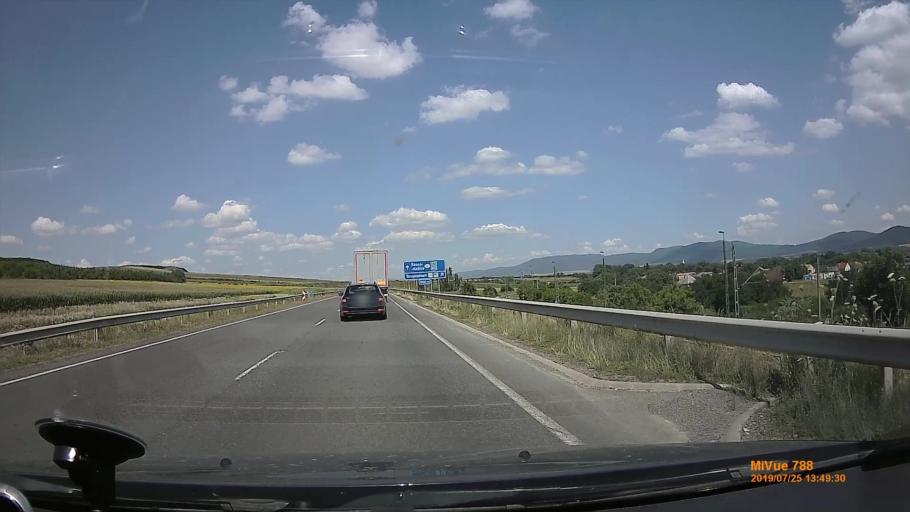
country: HU
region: Borsod-Abauj-Zemplen
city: Gonc
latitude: 48.5161
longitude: 21.2352
